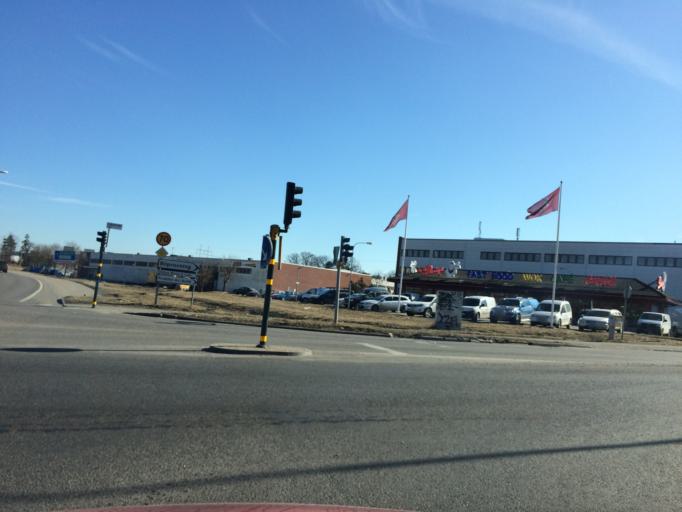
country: SE
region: Stockholm
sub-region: Huddinge Kommun
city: Segeltorp
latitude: 59.2879
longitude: 17.9370
